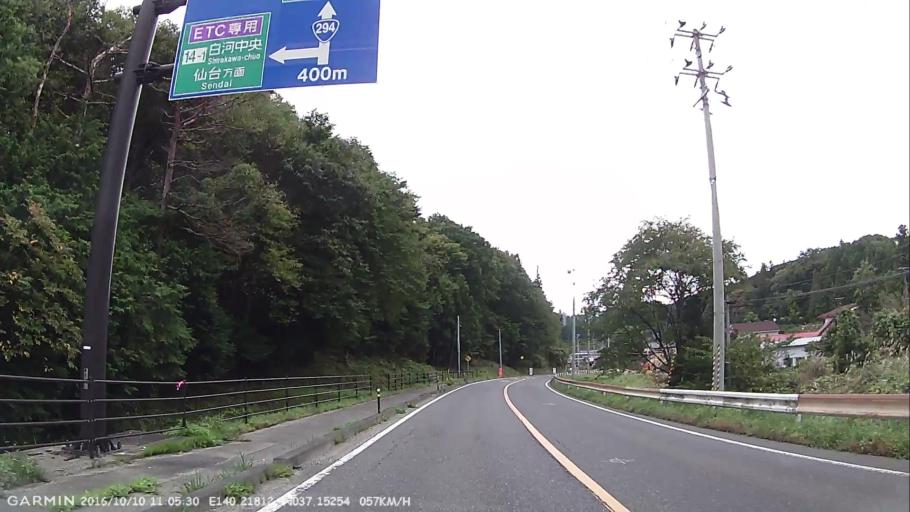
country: JP
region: Fukushima
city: Sukagawa
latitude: 37.1525
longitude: 140.2181
